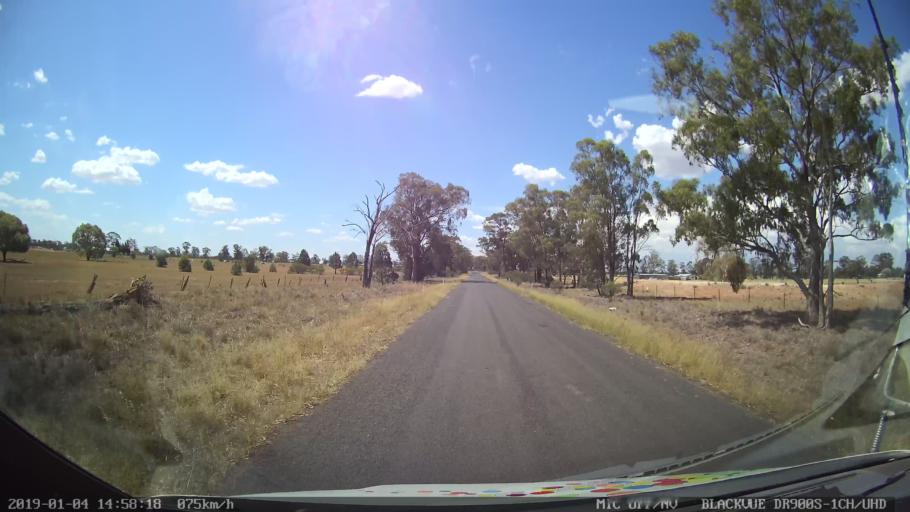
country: AU
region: New South Wales
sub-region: Gilgandra
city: Gilgandra
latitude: -31.9571
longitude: 148.6317
